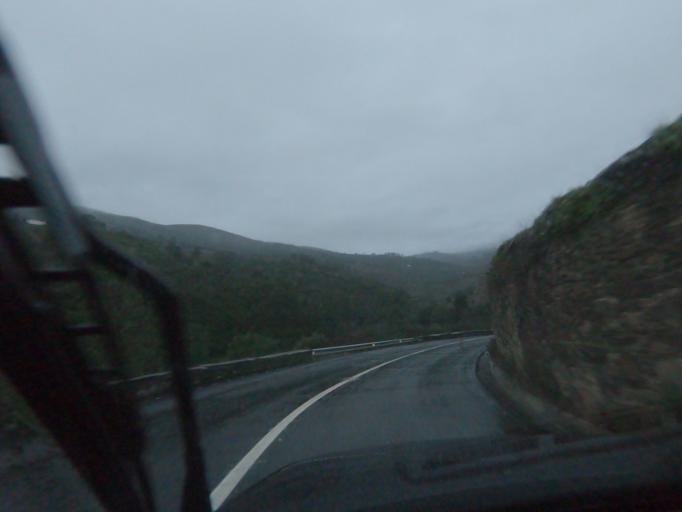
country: PT
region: Vila Real
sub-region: Sabrosa
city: Vilela
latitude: 41.2038
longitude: -7.5644
